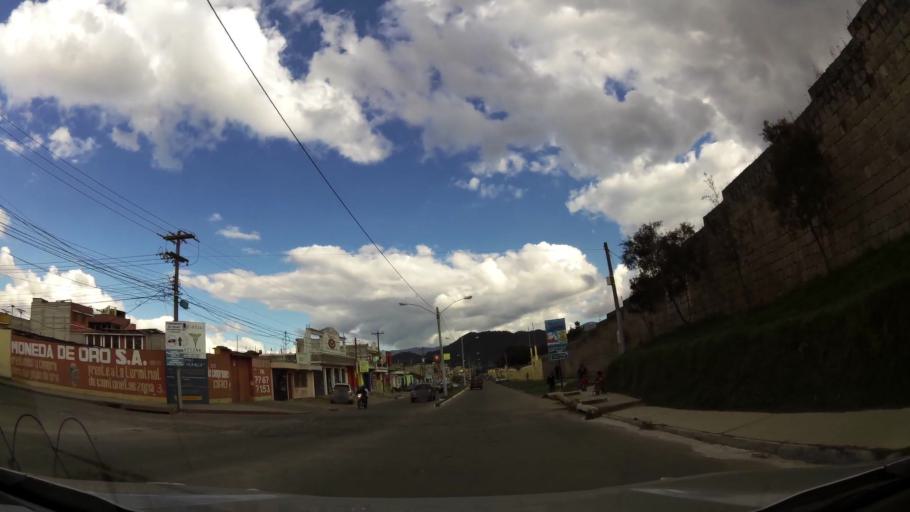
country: GT
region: Quetzaltenango
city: Quetzaltenango
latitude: 14.8383
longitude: -91.5299
